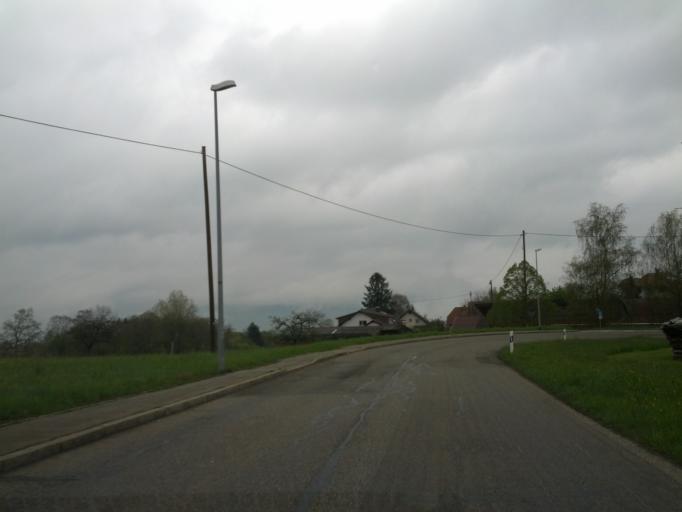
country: DE
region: Baden-Wuerttemberg
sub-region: Freiburg Region
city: Murg
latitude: 47.5974
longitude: 8.0275
